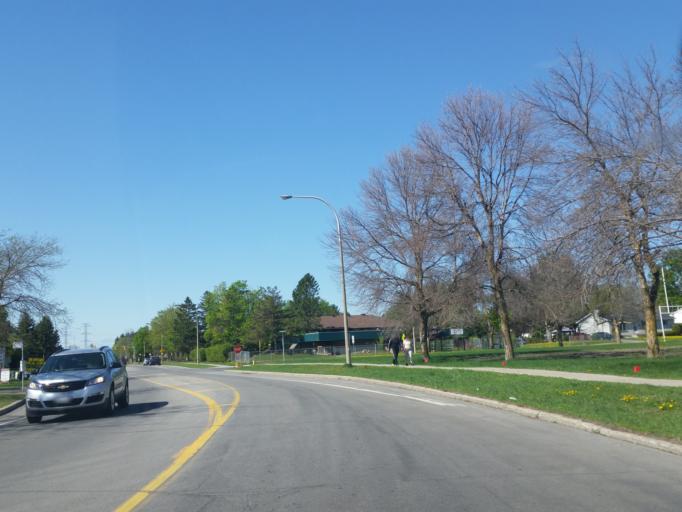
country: CA
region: Ontario
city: Ottawa
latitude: 45.3495
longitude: -75.7153
